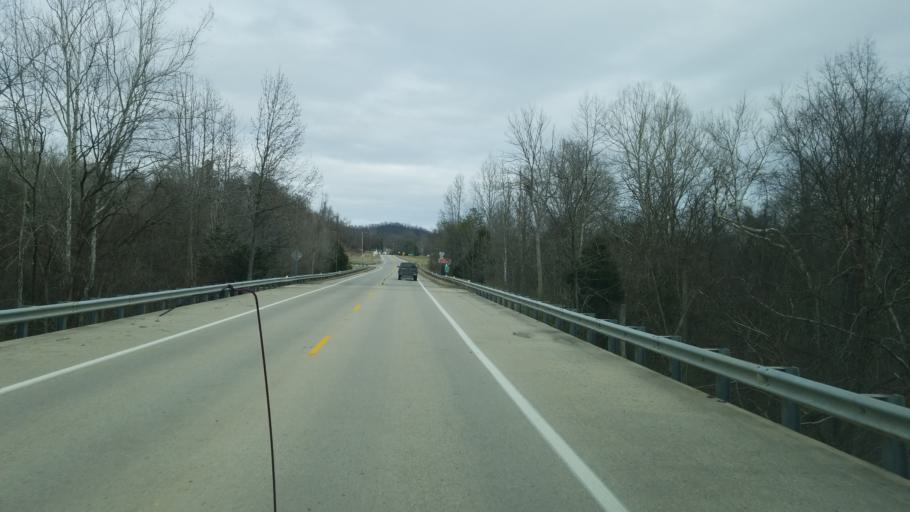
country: US
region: Ohio
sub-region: Scioto County
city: West Portsmouth
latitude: 38.6955
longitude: -83.1007
